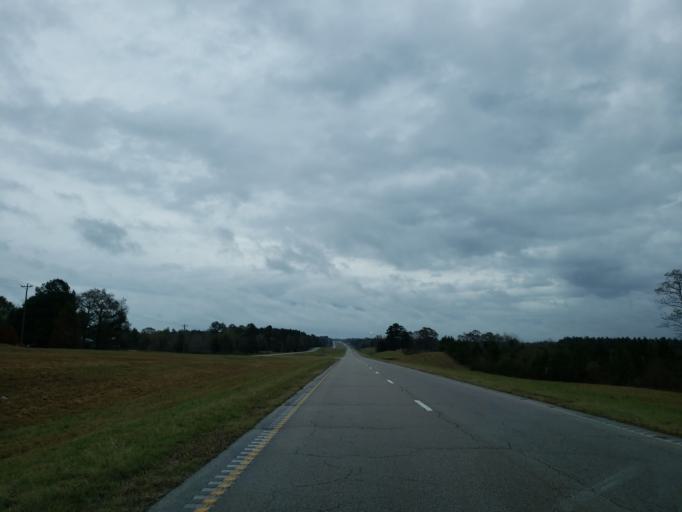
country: US
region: Mississippi
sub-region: Wayne County
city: Waynesboro
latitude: 31.6966
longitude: -88.8626
